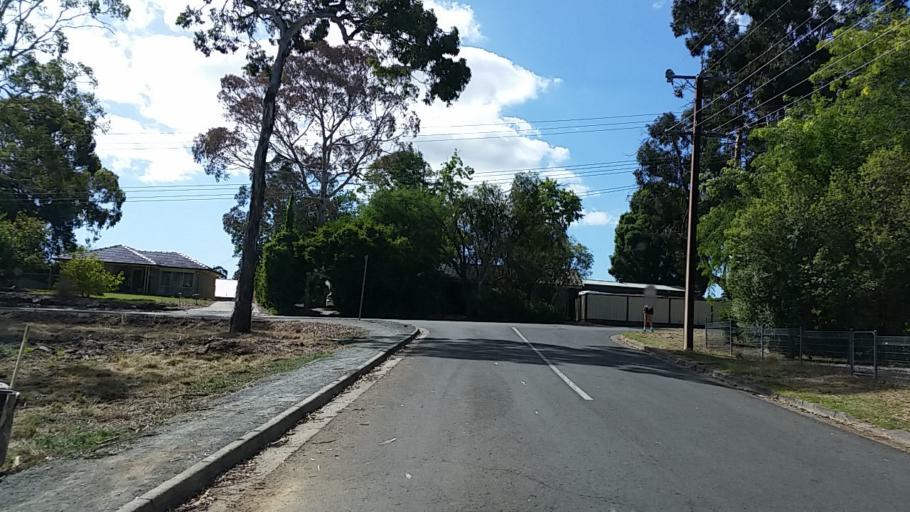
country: AU
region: South Australia
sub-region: Mount Barker
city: Hahndorf
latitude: -35.0267
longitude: 138.8151
